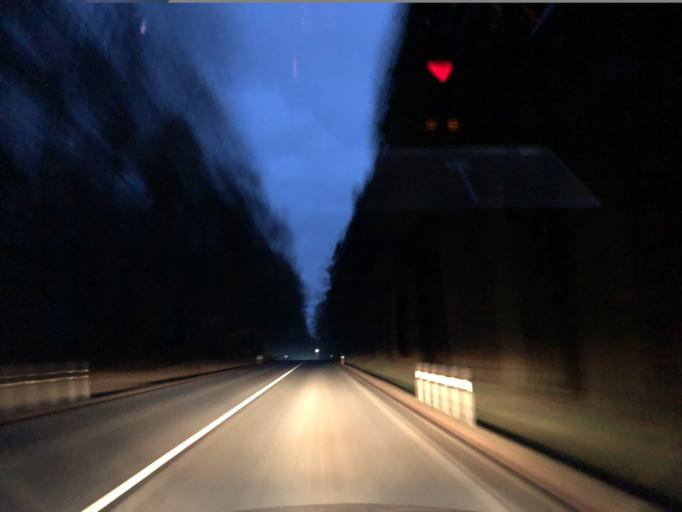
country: DE
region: Rheinland-Pfalz
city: Bettendorf
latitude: 50.2425
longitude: 7.8760
